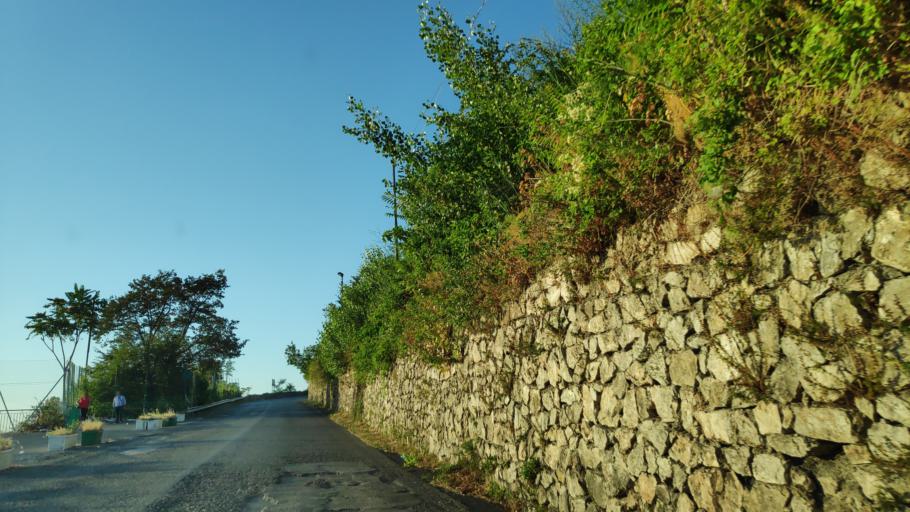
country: IT
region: Campania
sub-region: Provincia di Salerno
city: Corbara
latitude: 40.7237
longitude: 14.6017
